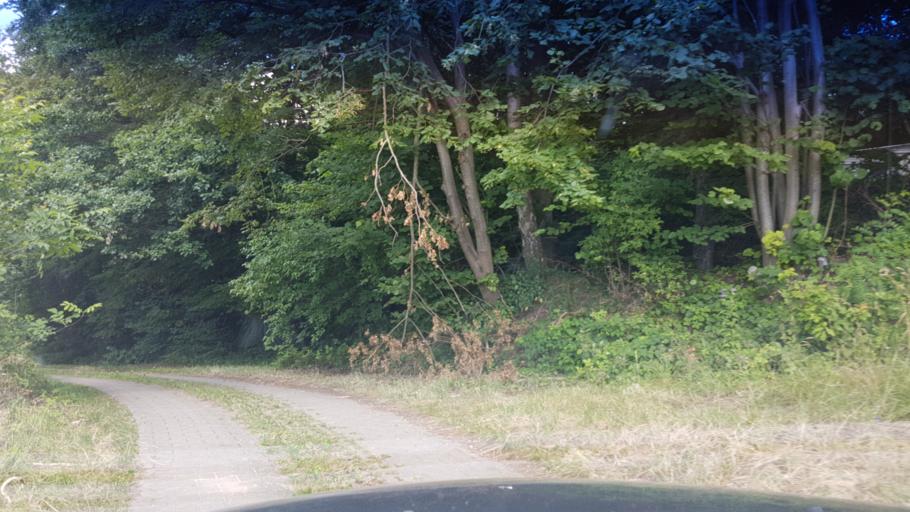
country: DE
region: Bavaria
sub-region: Upper Franconia
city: Schesslitz
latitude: 49.9460
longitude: 11.0563
